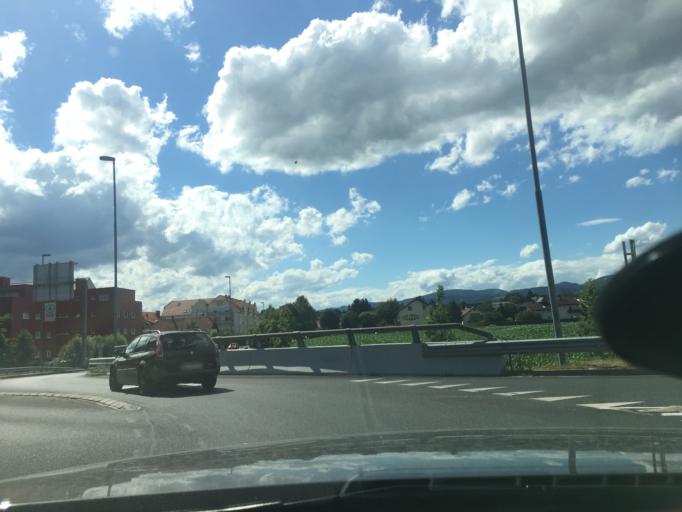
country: SI
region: Maribor
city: Pekre
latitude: 46.5378
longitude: 15.6154
